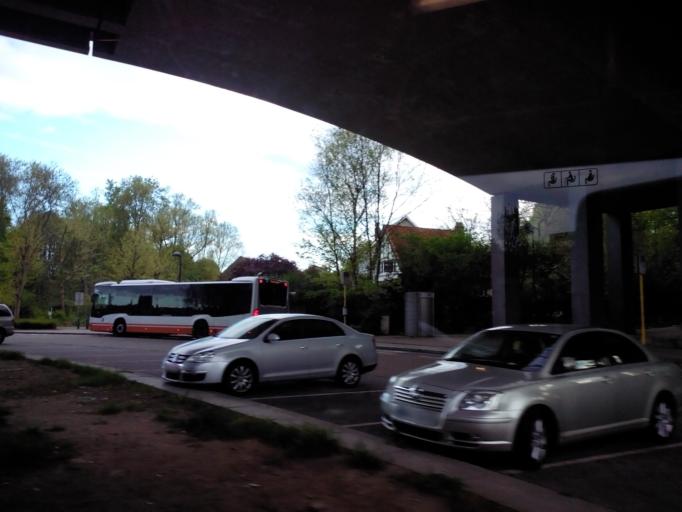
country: BE
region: Flanders
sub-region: Provincie Vlaams-Brabant
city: Kraainem
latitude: 50.8659
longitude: 4.4540
